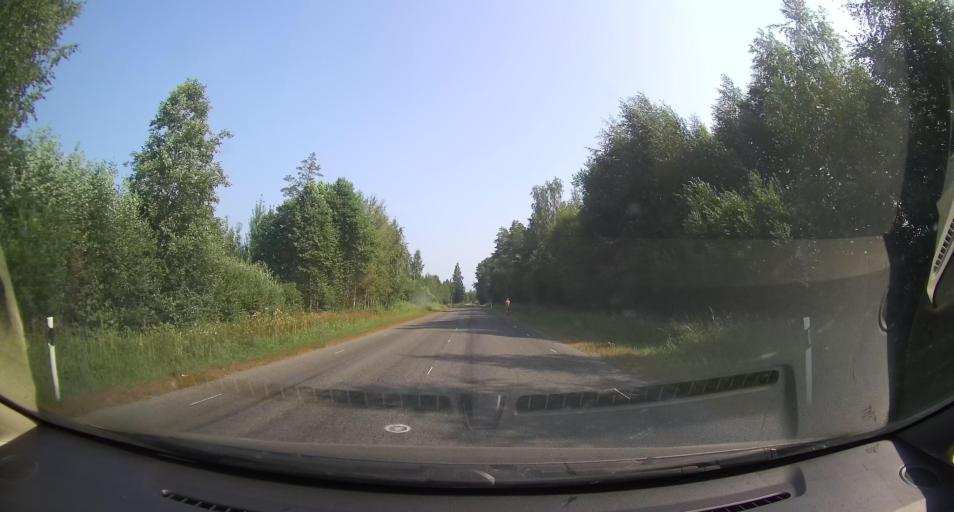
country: EE
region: Paernumaa
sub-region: Audru vald
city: Audru
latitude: 58.4500
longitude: 24.3134
